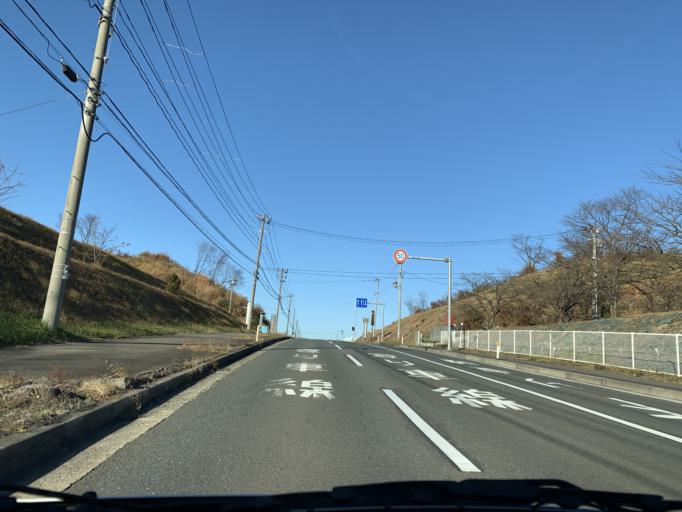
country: JP
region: Iwate
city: Mizusawa
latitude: 39.2038
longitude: 141.1777
